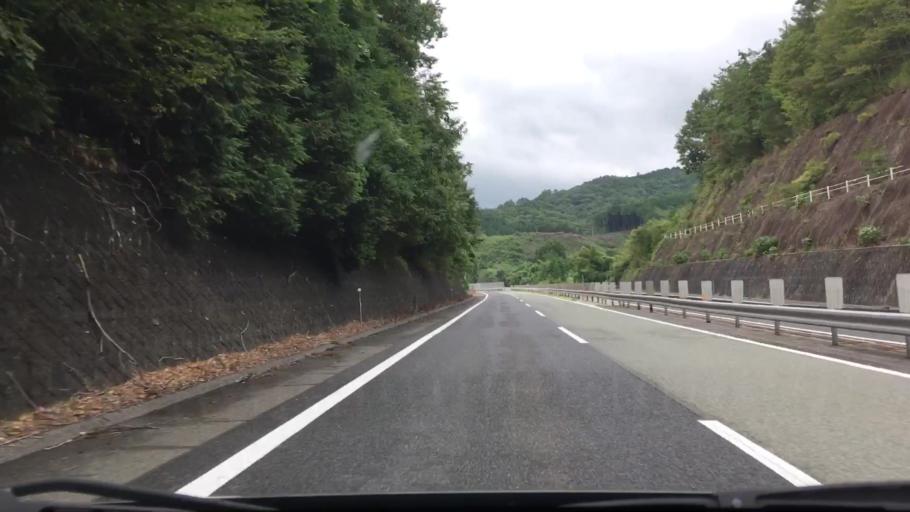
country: JP
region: Okayama
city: Niimi
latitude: 34.9435
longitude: 133.3291
